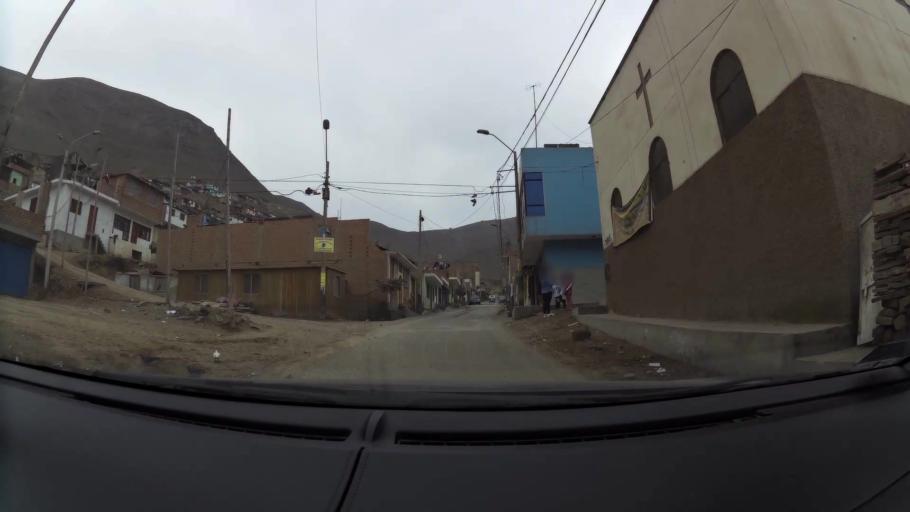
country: PE
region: Lima
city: Ventanilla
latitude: -11.9168
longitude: -77.0930
